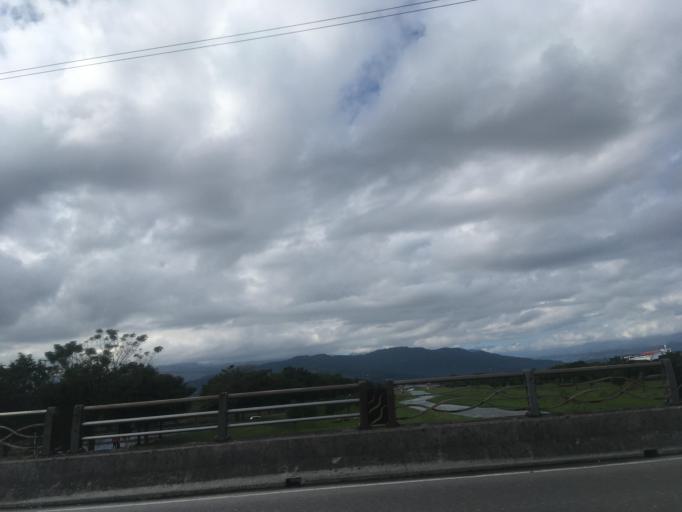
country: TW
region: Taiwan
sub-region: Yilan
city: Yilan
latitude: 24.6910
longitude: 121.7333
